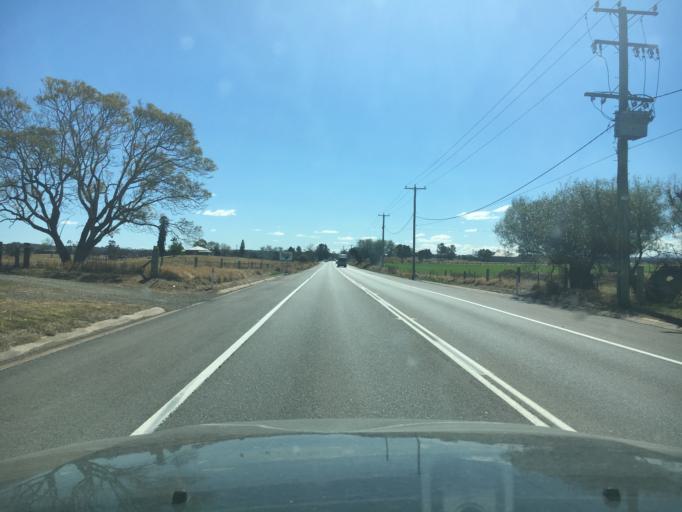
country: AU
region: New South Wales
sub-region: Singleton
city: Singleton
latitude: -32.5851
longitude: 151.1907
